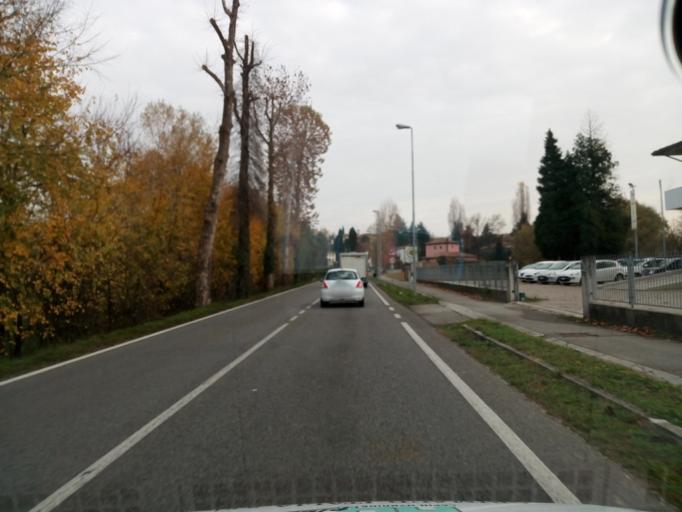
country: IT
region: Veneto
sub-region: Provincia di Treviso
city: One
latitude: 45.7813
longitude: 11.8597
